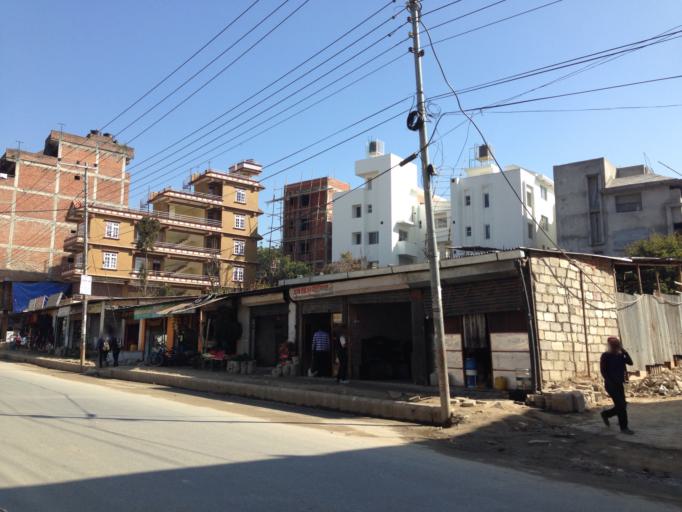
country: NP
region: Central Region
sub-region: Bagmati Zone
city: Kathmandu
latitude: 27.7559
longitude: 85.3488
